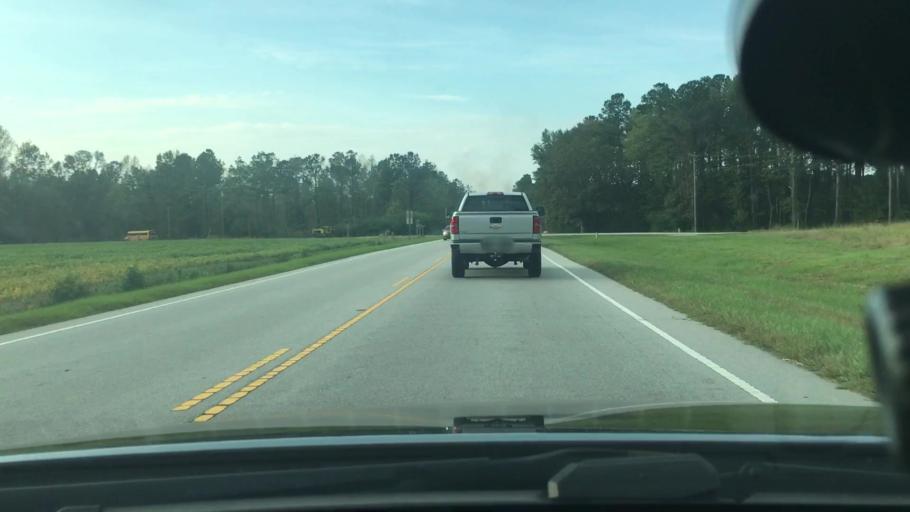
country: US
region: North Carolina
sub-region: Craven County
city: Vanceboro
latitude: 35.3086
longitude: -77.1373
